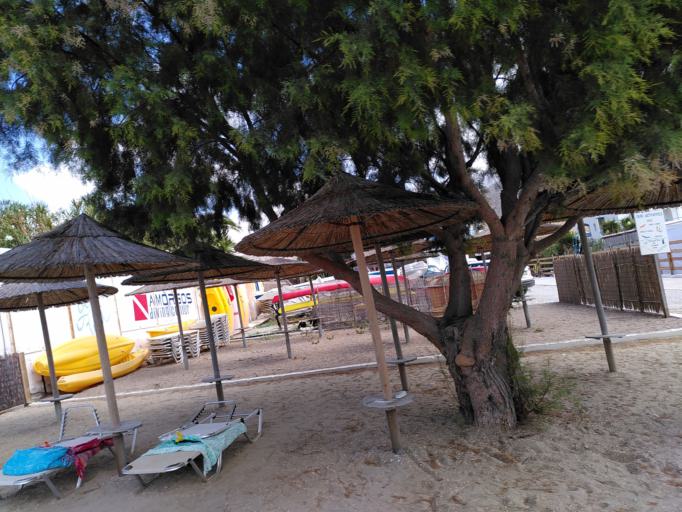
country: GR
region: South Aegean
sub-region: Nomos Kykladon
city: Amorgos
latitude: 36.9036
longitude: 25.9780
